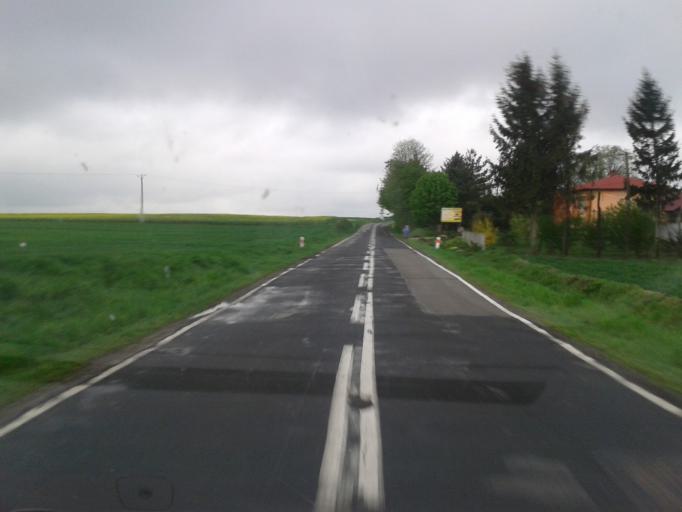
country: PL
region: Lublin Voivodeship
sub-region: Powiat hrubieszowski
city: Dolhobyczow
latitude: 50.5734
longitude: 23.9637
